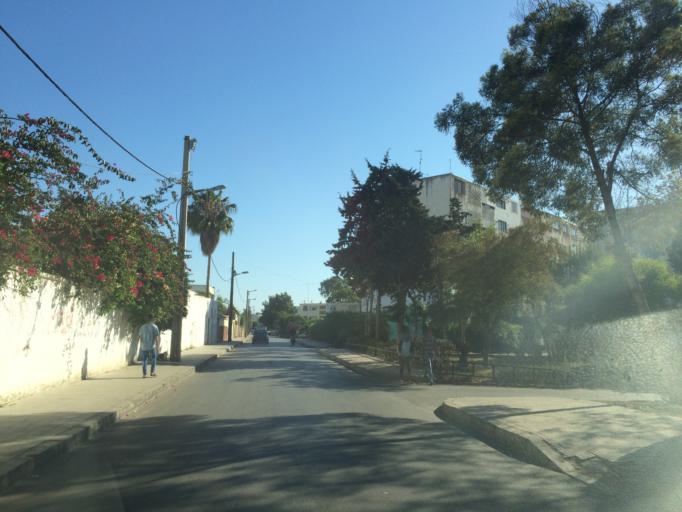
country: MA
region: Rabat-Sale-Zemmour-Zaer
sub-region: Rabat
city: Rabat
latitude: 33.9937
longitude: -6.8191
